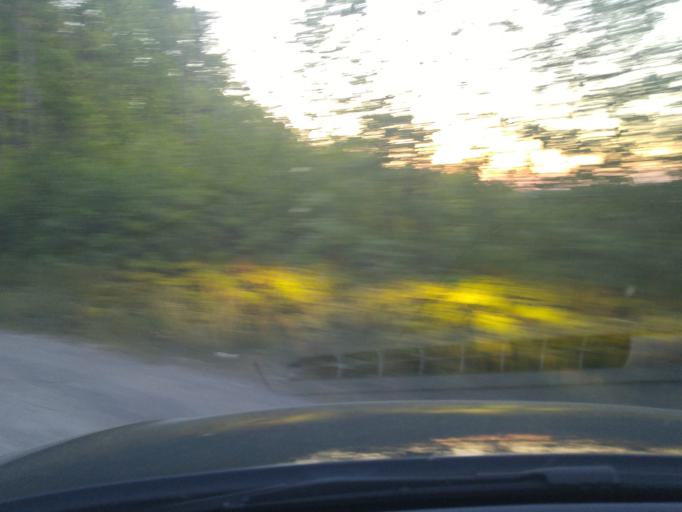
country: DE
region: Baden-Wuerttemberg
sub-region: Regierungsbezirk Stuttgart
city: Cleebronn
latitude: 49.0351
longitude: 9.0419
